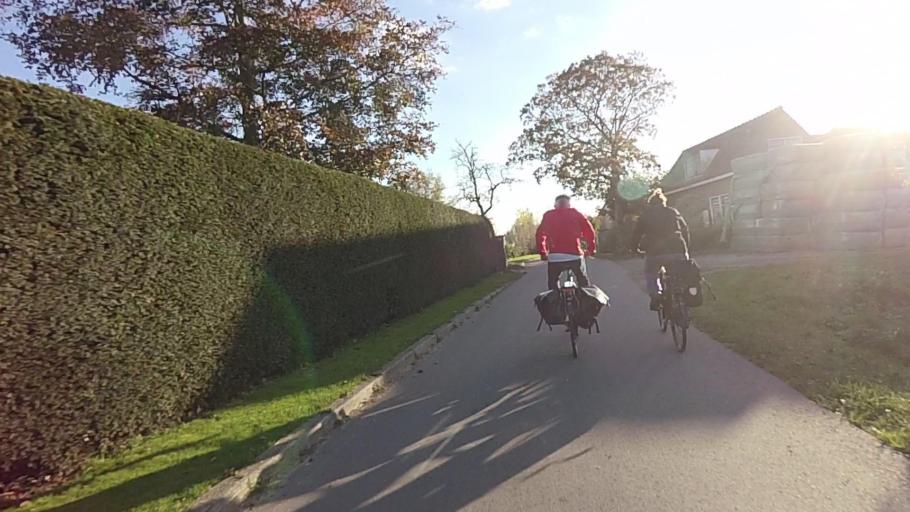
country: NL
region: Utrecht
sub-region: Stichtse Vecht
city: Vreeland
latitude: 52.2594
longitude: 5.0317
